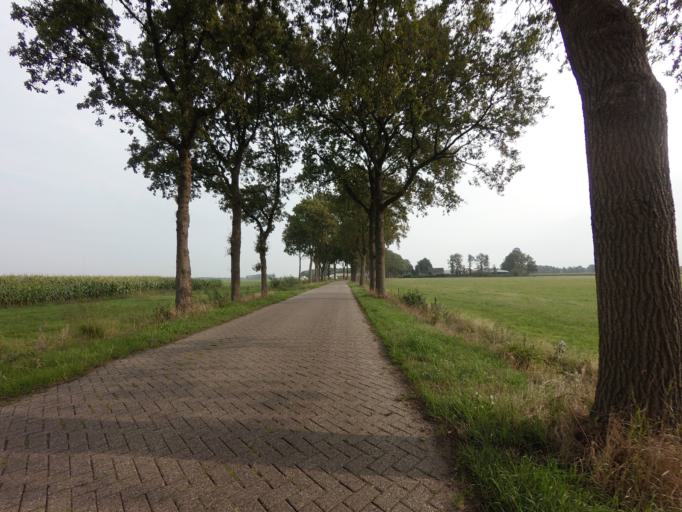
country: NL
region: Drenthe
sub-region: Gemeente Westerveld
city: Dwingeloo
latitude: 52.8662
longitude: 6.4241
